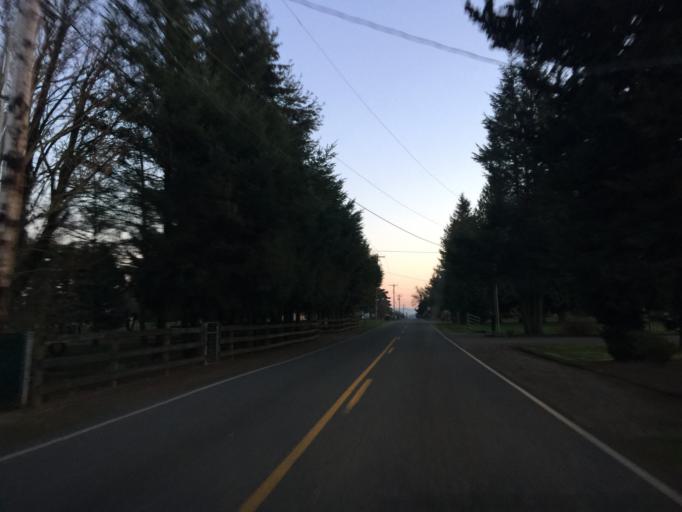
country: US
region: Washington
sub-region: Whatcom County
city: Lynden
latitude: 48.9624
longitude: -122.4076
